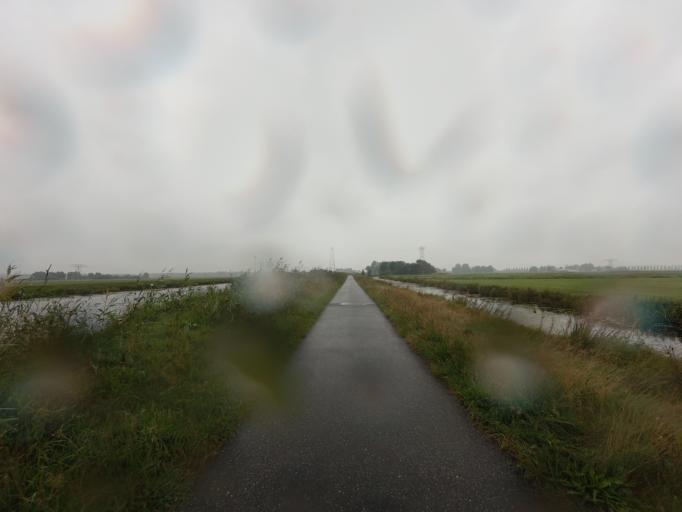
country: NL
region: Friesland
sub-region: Gemeente Boarnsterhim
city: Aldeboarn
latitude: 53.0082
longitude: 5.8890
